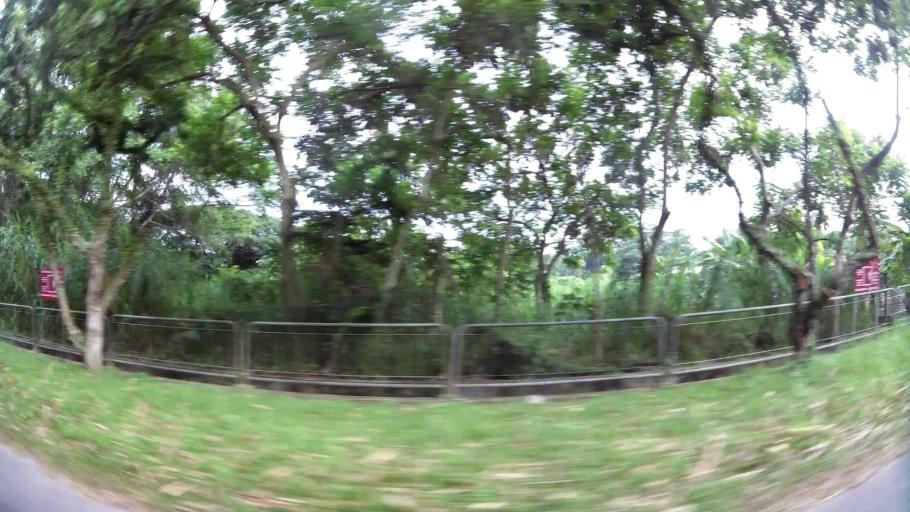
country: MY
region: Johor
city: Johor Bahru
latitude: 1.4363
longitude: 103.7137
